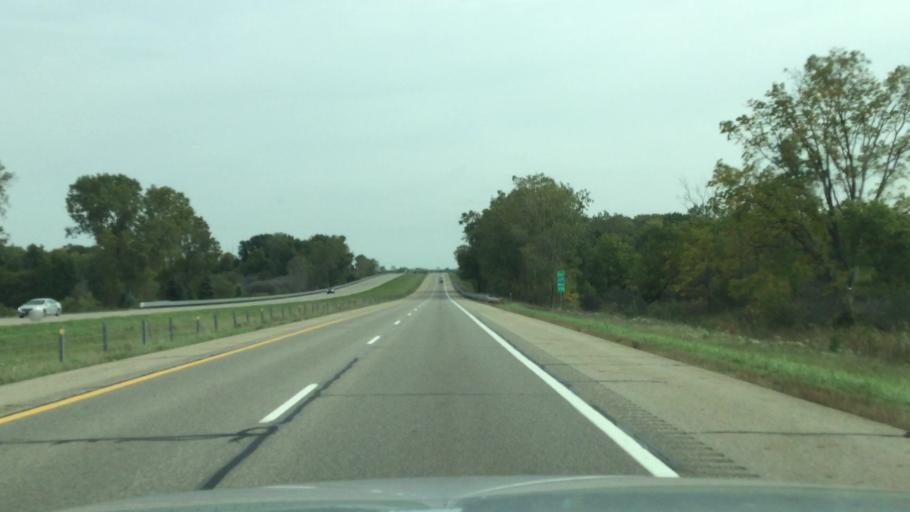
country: US
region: Michigan
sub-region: Shiawassee County
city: Durand
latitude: 42.9146
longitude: -84.0397
